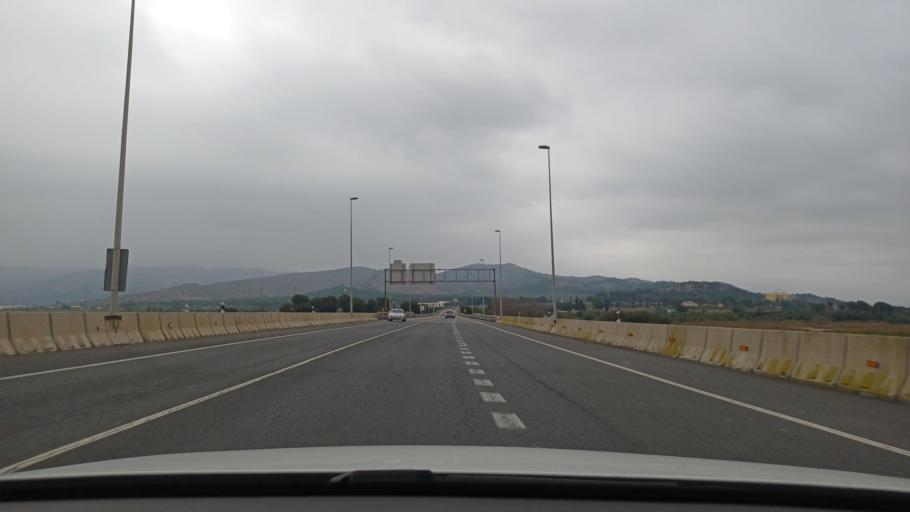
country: ES
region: Valencia
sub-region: Provincia de Castello
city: Borriol
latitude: 39.9955
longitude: -0.0892
